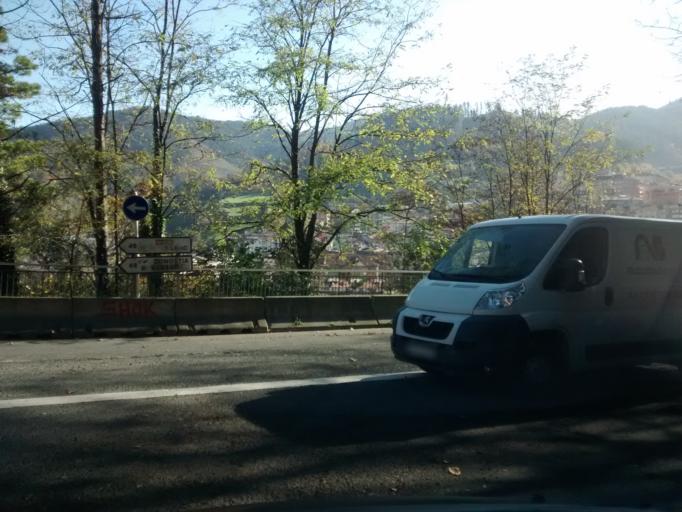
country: ES
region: Basque Country
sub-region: Provincia de Guipuzcoa
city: Eibar
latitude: 43.1869
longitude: -2.4733
